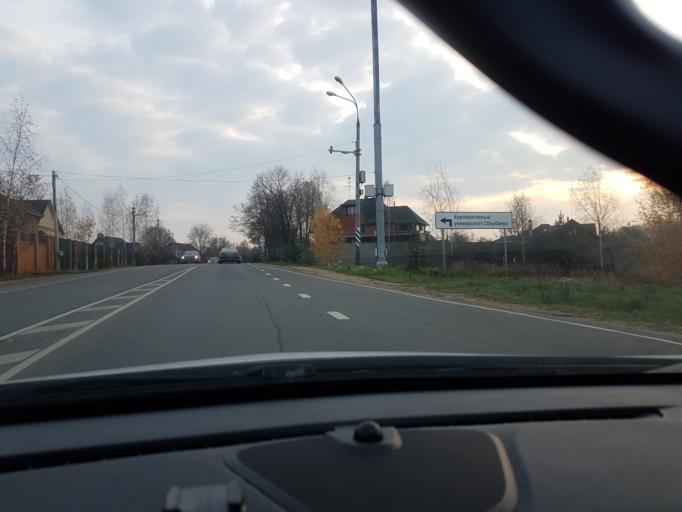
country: RU
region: Moskovskaya
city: Snegiri
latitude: 55.8431
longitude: 36.9960
